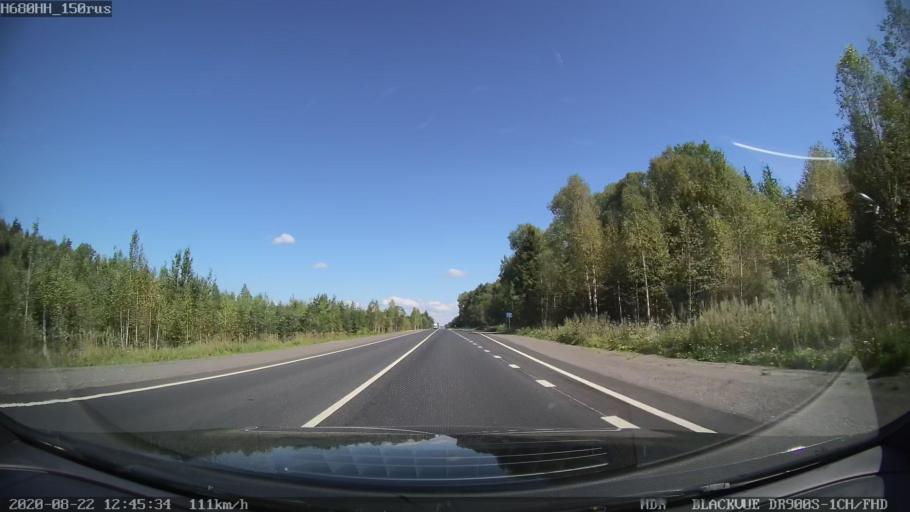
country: RU
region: Tverskaya
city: Rameshki
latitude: 57.4070
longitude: 36.1243
